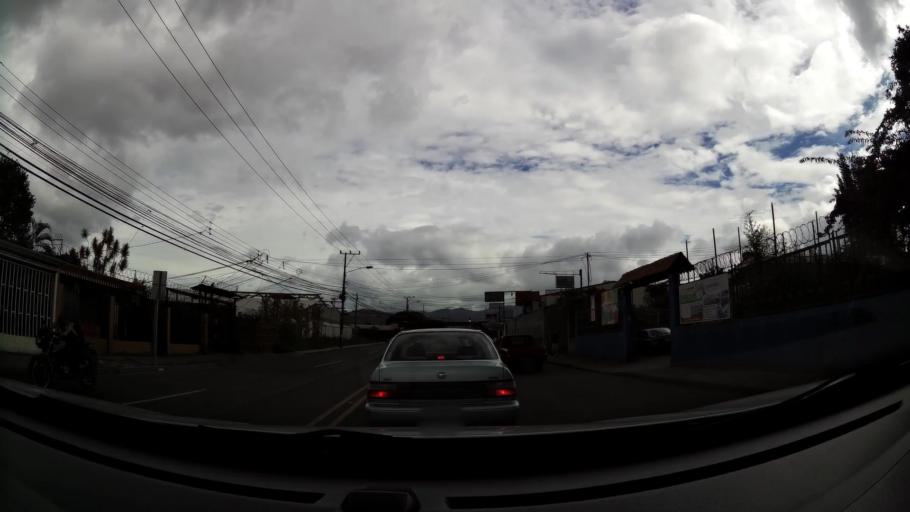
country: CR
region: San Jose
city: Alajuelita
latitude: 9.8955
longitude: -84.0844
